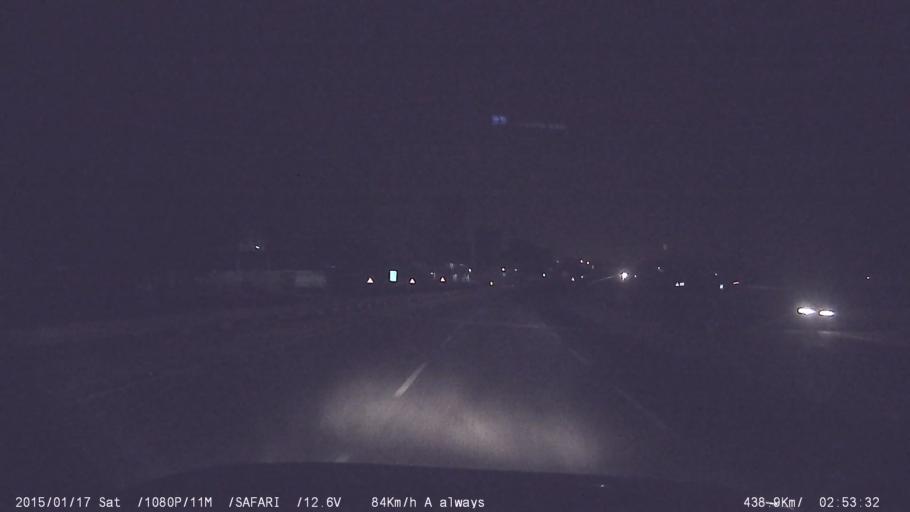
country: IN
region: Karnataka
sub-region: Bangalore Urban
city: Anekal
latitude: 12.7862
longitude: 77.7483
